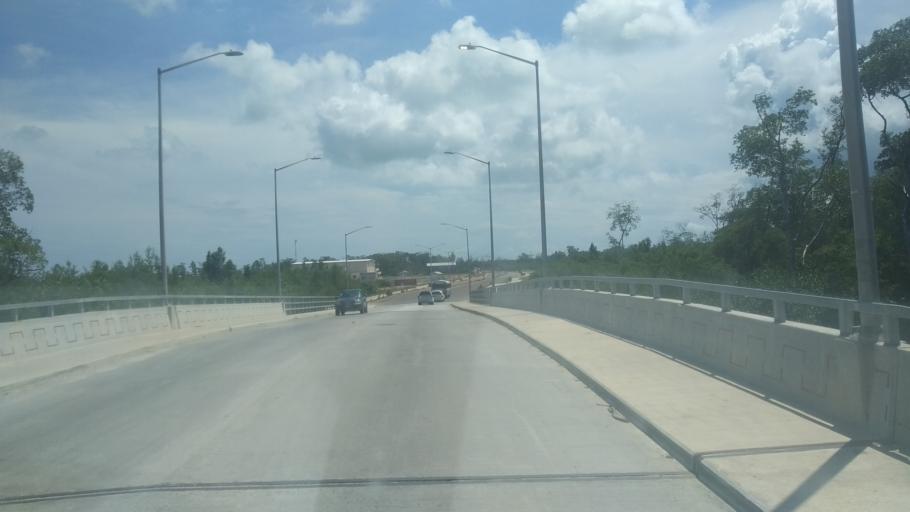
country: BZ
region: Belize
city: Belize City
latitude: 17.5080
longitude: -88.2215
